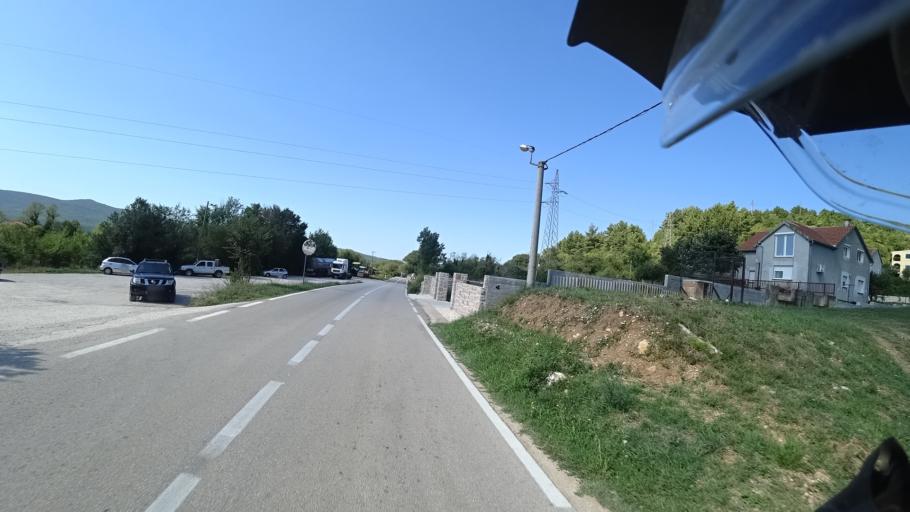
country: HR
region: Sibensko-Kniniska
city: Drnis
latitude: 43.8676
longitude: 16.1903
